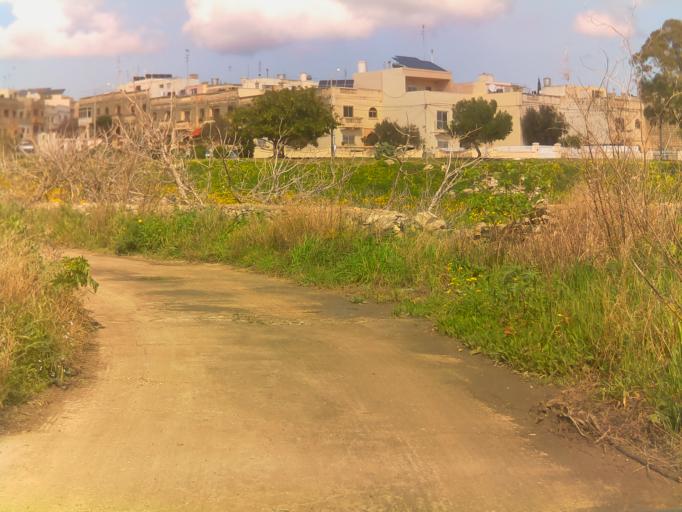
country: MT
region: Saint Lucia
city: Santa Lucija
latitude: 35.8591
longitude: 14.5013
